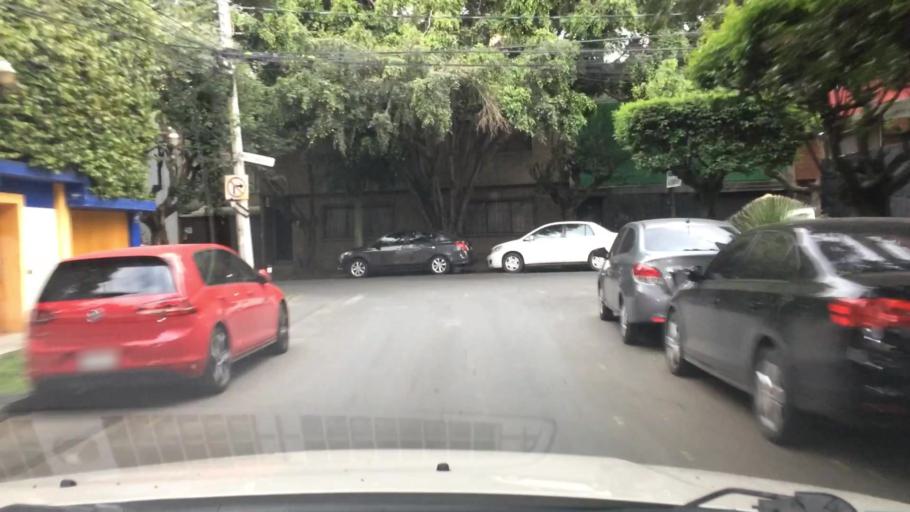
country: MX
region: Mexico City
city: Alvaro Obregon
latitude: 19.3544
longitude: -99.1893
